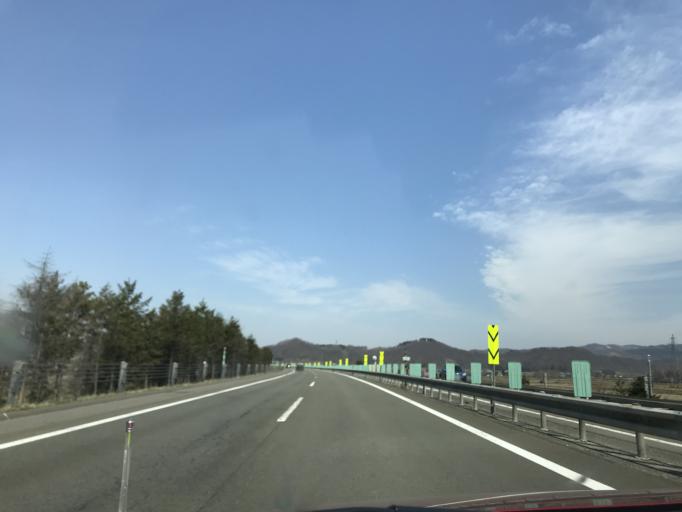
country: JP
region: Hokkaido
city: Iwamizawa
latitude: 43.2256
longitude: 141.8302
